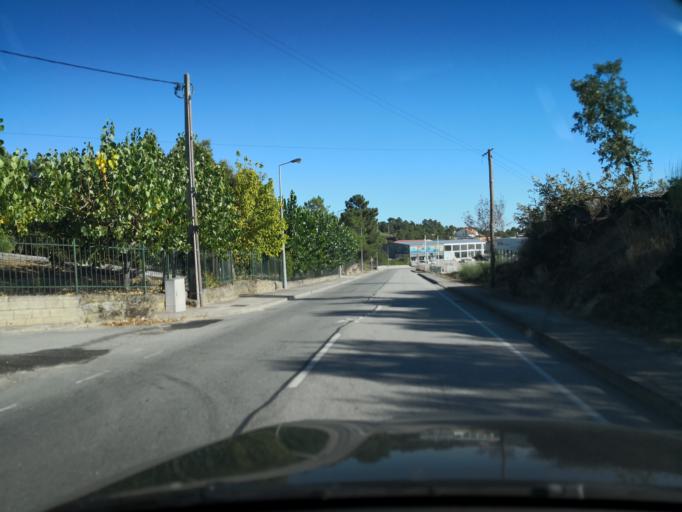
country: PT
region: Vila Real
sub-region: Valpacos
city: Valpacos
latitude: 41.6304
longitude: -7.3148
